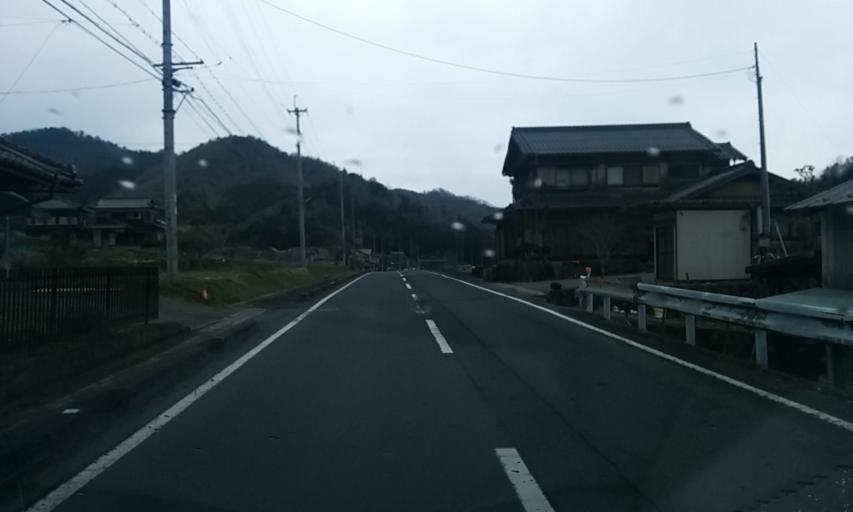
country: JP
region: Hyogo
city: Sasayama
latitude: 35.1273
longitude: 135.4117
